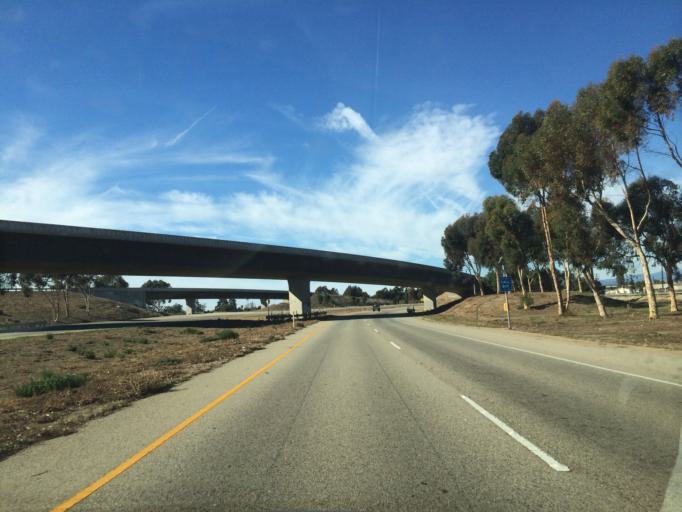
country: US
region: California
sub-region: Ventura County
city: Oxnard
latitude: 34.1610
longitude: -119.1367
